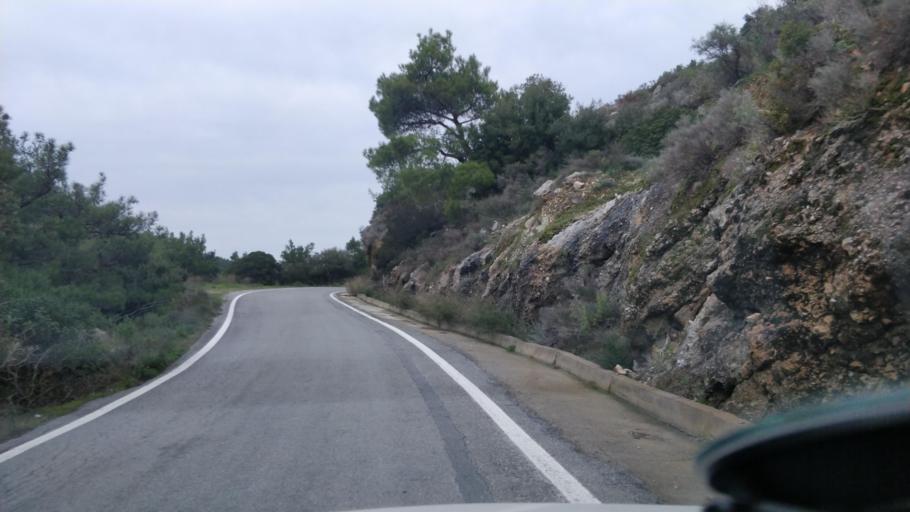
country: GR
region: Crete
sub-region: Nomos Lasithiou
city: Kritsa
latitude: 35.0970
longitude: 25.6981
